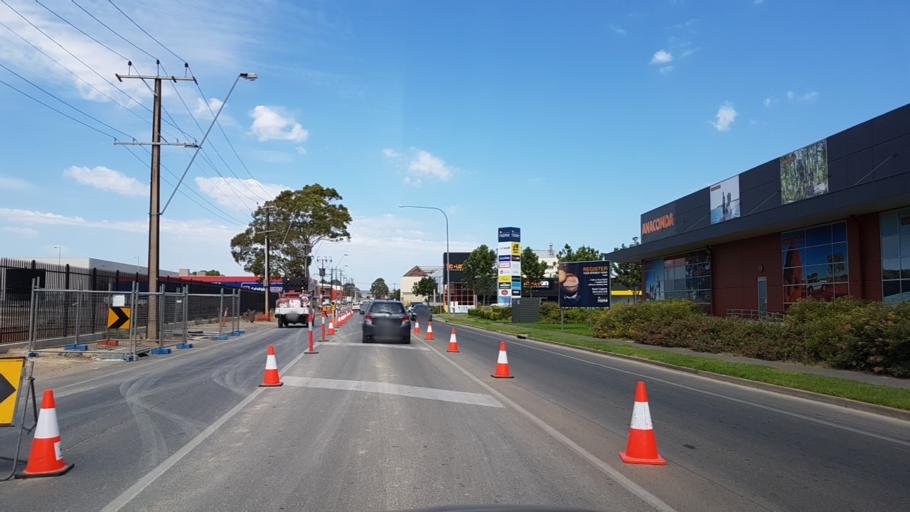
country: AU
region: South Australia
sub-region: Unley
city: Forestville
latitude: -34.9337
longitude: 138.5767
